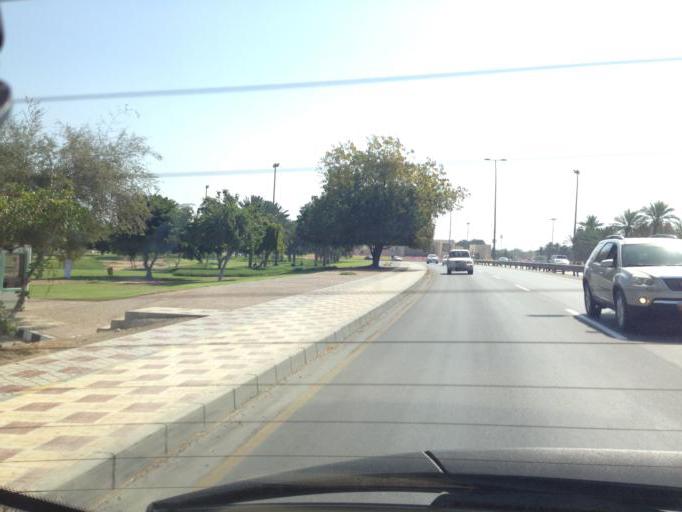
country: OM
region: Muhafazat Masqat
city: As Sib al Jadidah
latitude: 23.5873
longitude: 58.2491
